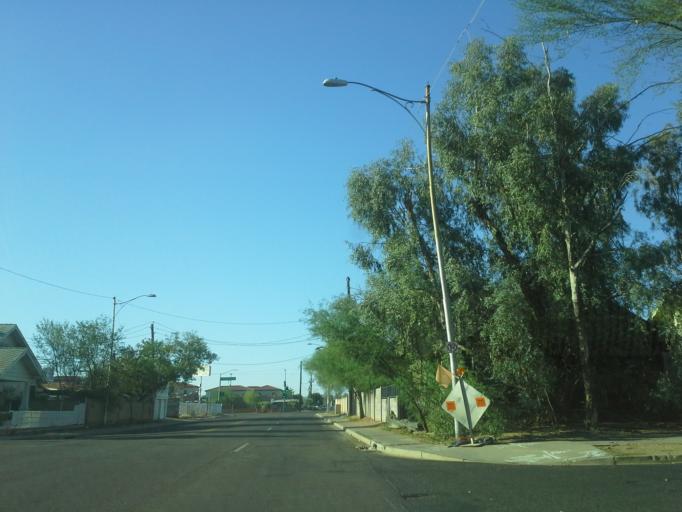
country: US
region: Arizona
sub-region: Maricopa County
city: Phoenix
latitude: 33.4501
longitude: -112.0914
